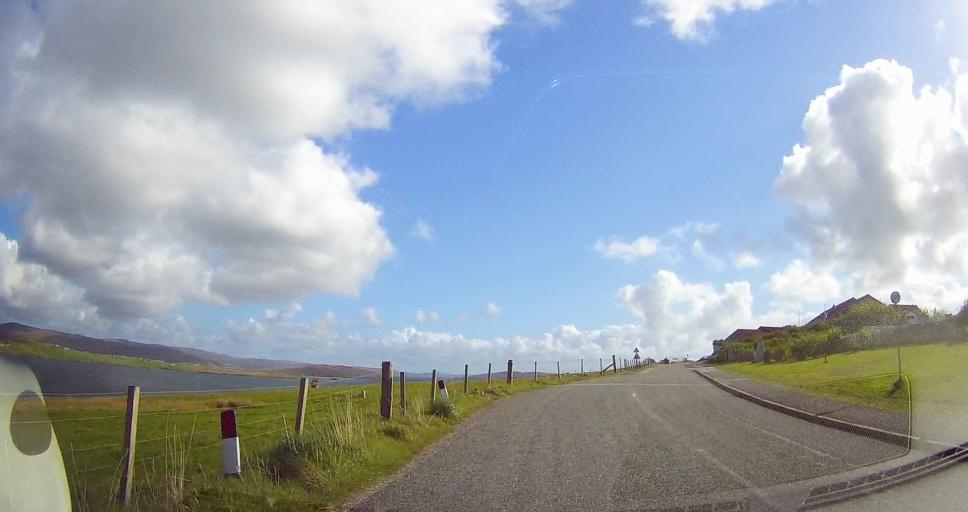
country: GB
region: Scotland
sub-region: Shetland Islands
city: Lerwick
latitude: 60.3904
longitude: -1.3695
